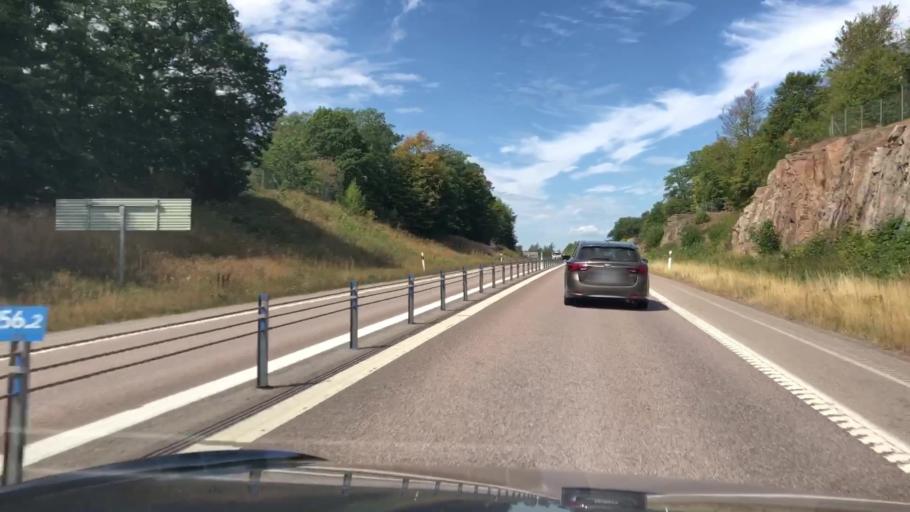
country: SE
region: Blekinge
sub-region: Ronneby Kommun
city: Kallinge
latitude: 56.2258
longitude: 15.2732
